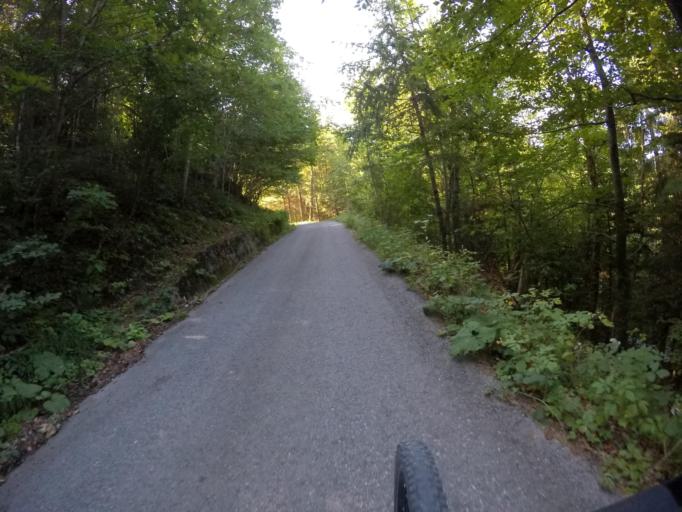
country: IT
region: Friuli Venezia Giulia
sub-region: Provincia di Udine
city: Zuglio
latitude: 46.4416
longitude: 13.0851
